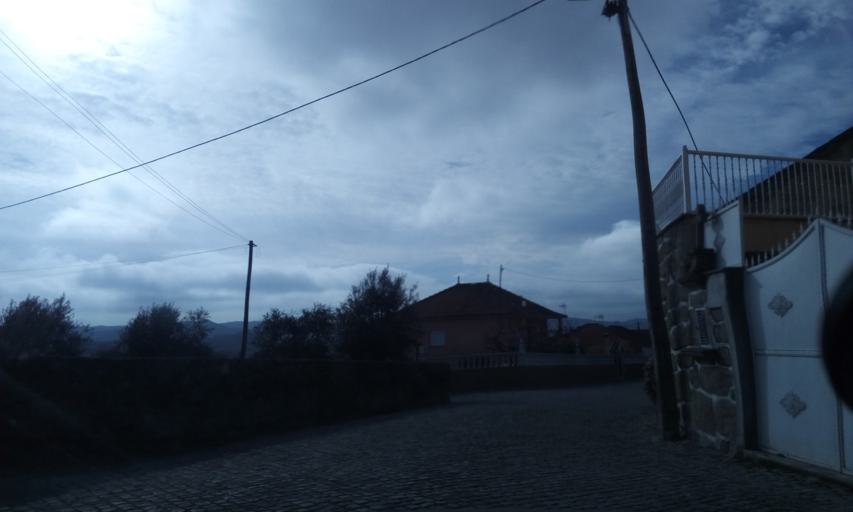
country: PT
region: Guarda
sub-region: Aguiar da Beira
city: Aguiar da Beira
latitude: 40.7312
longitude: -7.5564
